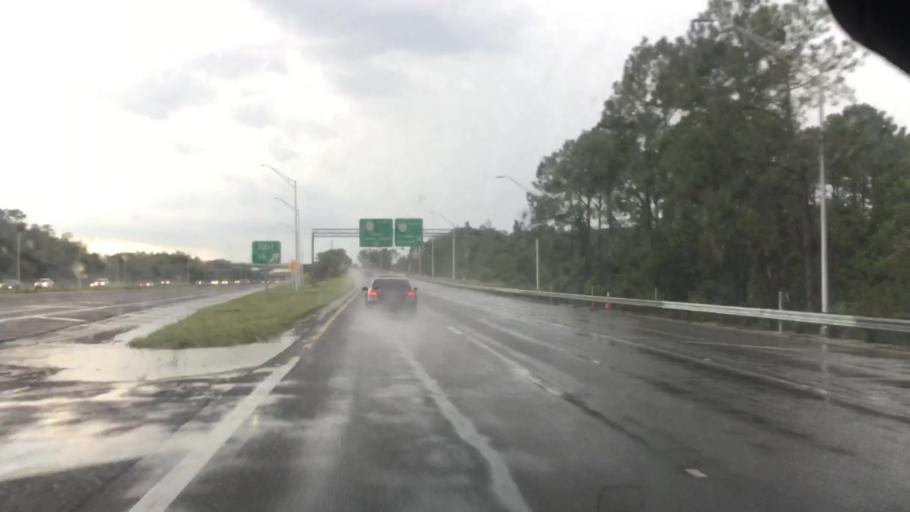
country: US
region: Florida
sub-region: Orange County
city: Alafaya
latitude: 28.4517
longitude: -81.2211
